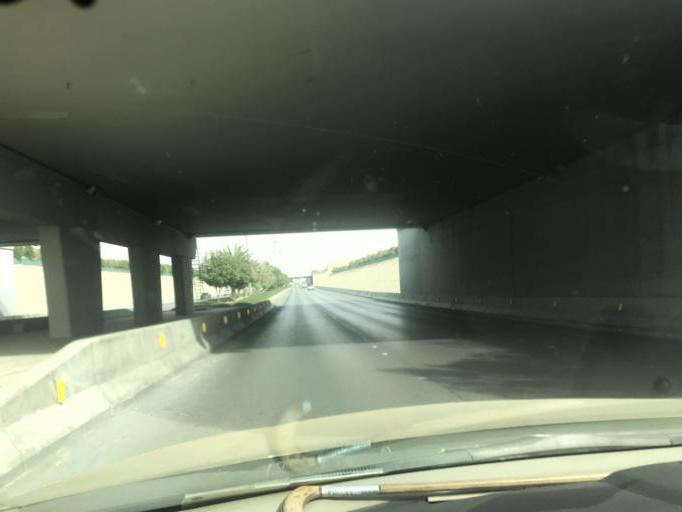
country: SA
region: Ar Riyad
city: Riyadh
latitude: 24.6673
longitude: 46.7928
